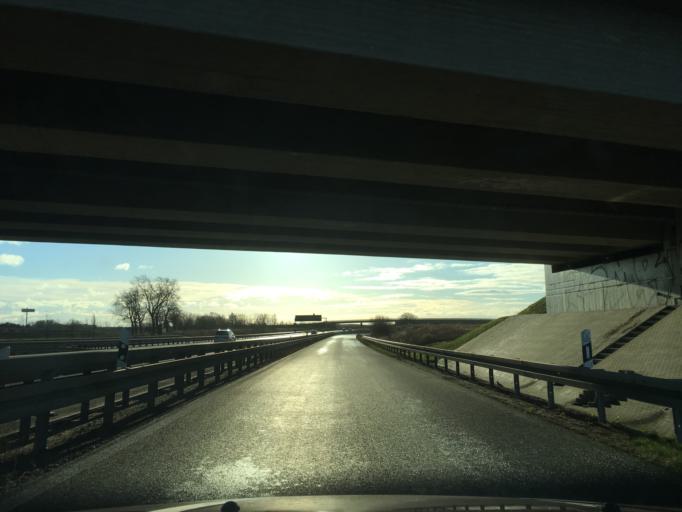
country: DE
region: Brandenburg
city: Schonefeld
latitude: 52.3736
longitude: 13.5462
